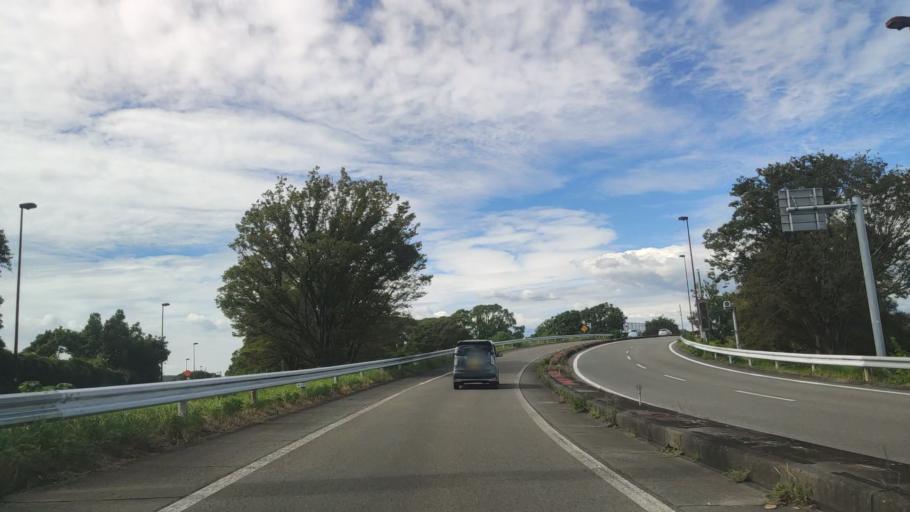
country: JP
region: Shizuoka
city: Hamamatsu
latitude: 34.7639
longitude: 137.6799
